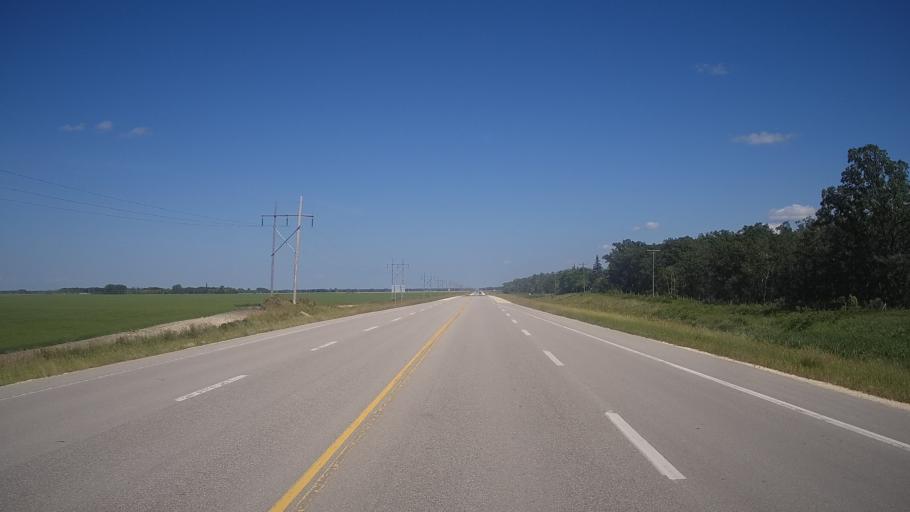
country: CA
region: Manitoba
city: Stonewall
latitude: 50.1227
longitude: -97.4358
